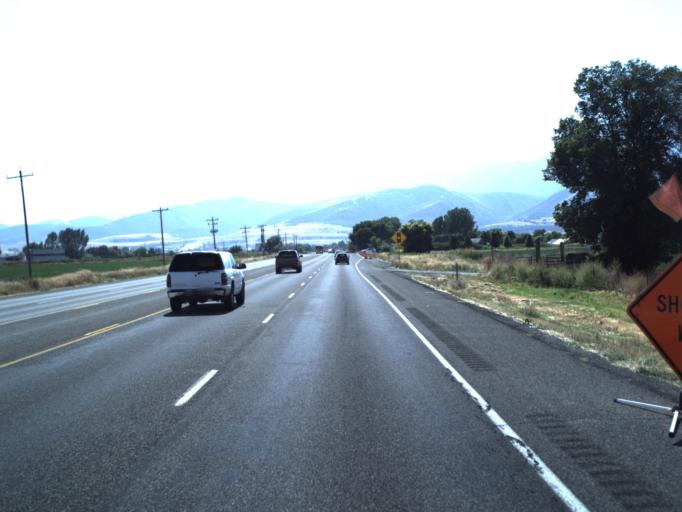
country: US
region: Utah
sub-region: Cache County
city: Wellsville
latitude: 41.6515
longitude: -111.9075
